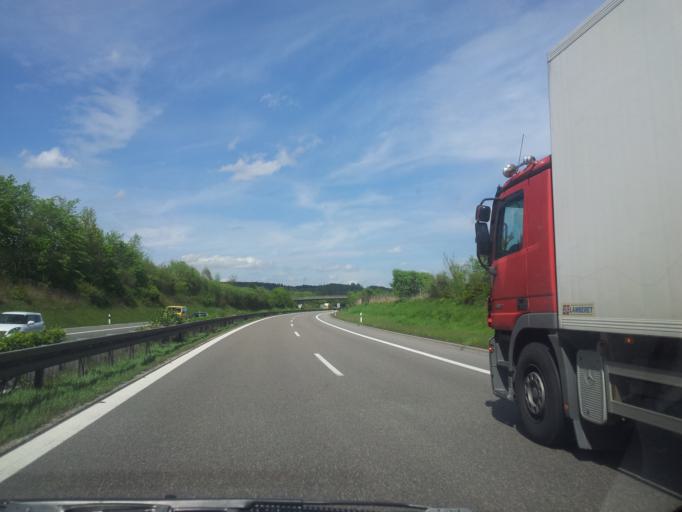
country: DE
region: Baden-Wuerttemberg
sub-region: Tuebingen Region
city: Leutkirch im Allgau
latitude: 47.8496
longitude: 9.9927
